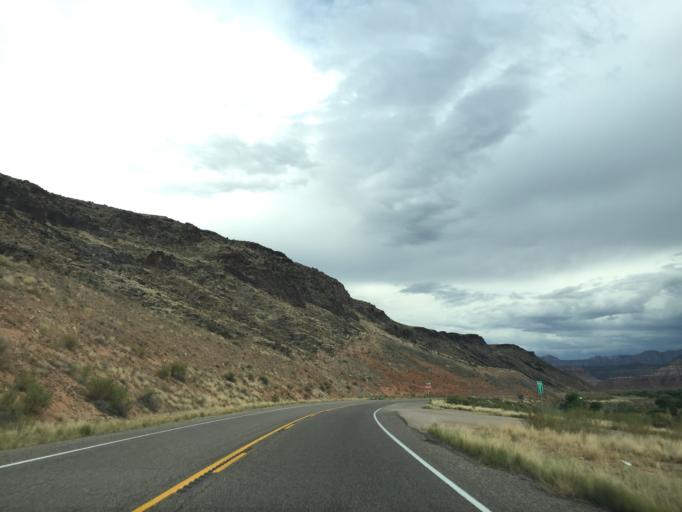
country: US
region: Utah
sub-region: Washington County
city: LaVerkin
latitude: 37.1949
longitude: -113.1478
